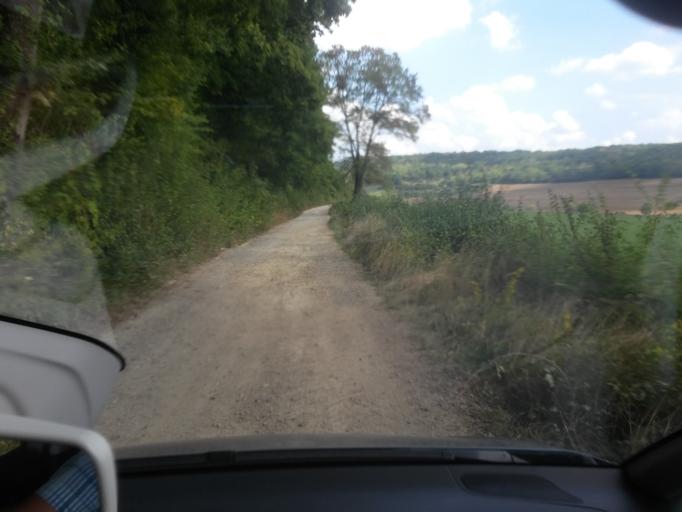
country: FR
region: Lorraine
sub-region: Departement de la Meuse
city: Montmedy
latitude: 49.5036
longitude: 5.3921
